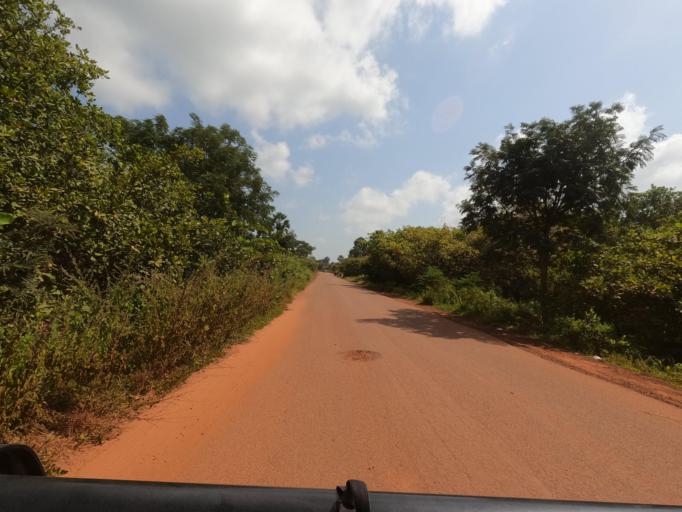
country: GW
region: Oio
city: Bissora
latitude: 12.2869
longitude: -15.7769
